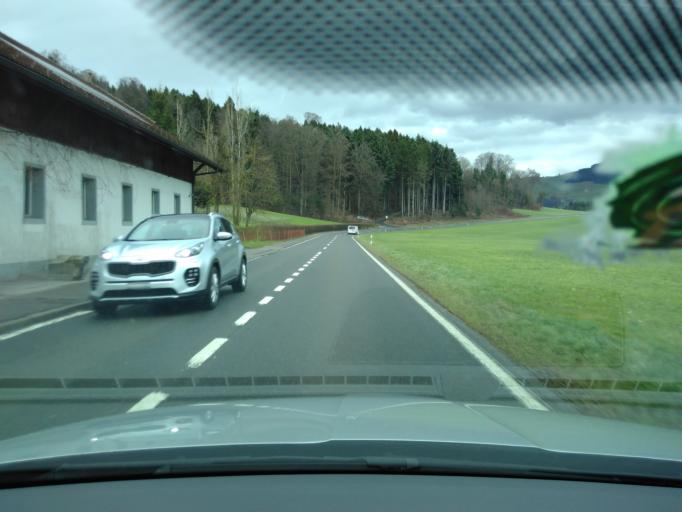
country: CH
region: Lucerne
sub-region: Hochdorf District
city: Inwil
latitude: 47.1235
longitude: 8.3616
